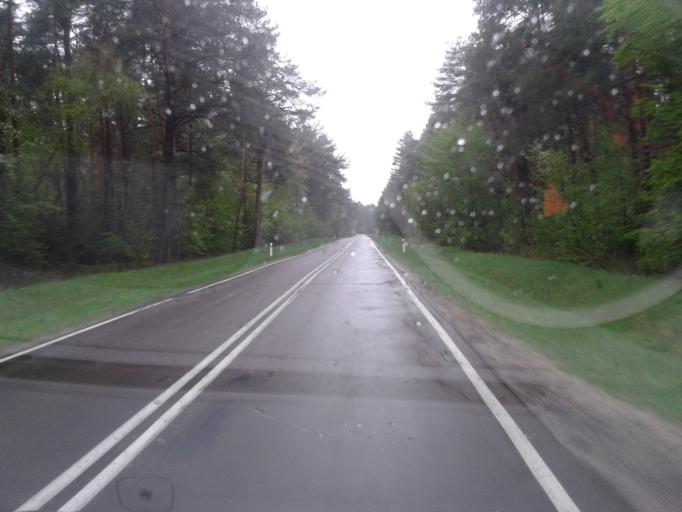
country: PL
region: Subcarpathian Voivodeship
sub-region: Powiat lubaczowski
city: Narol
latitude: 50.3691
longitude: 23.3608
